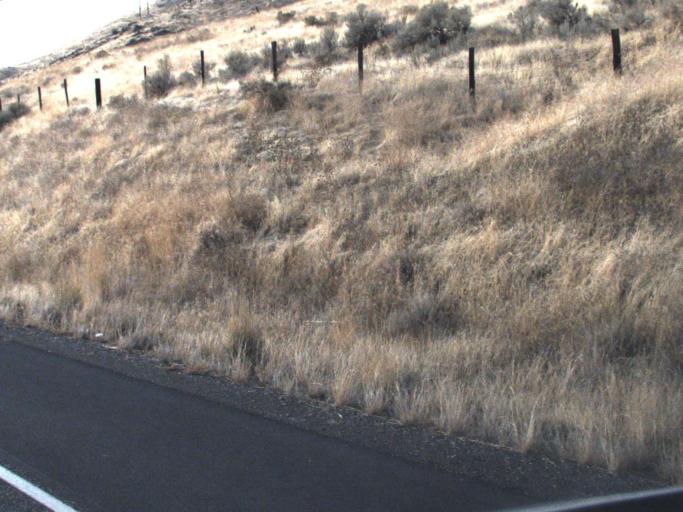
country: US
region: Washington
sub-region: Asotin County
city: Clarkston Heights-Vineland
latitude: 46.4060
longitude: -117.2253
